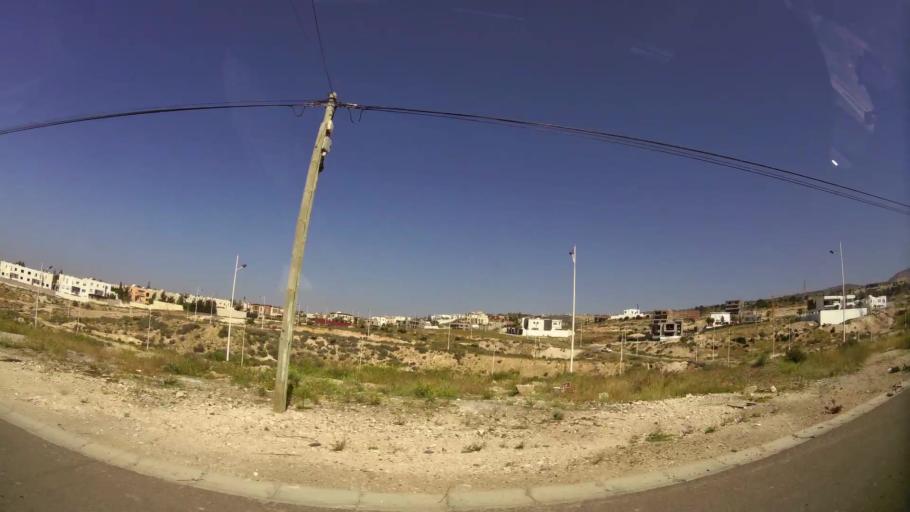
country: MA
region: Souss-Massa-Draa
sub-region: Agadir-Ida-ou-Tnan
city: Agadir
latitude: 30.4407
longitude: -9.5762
